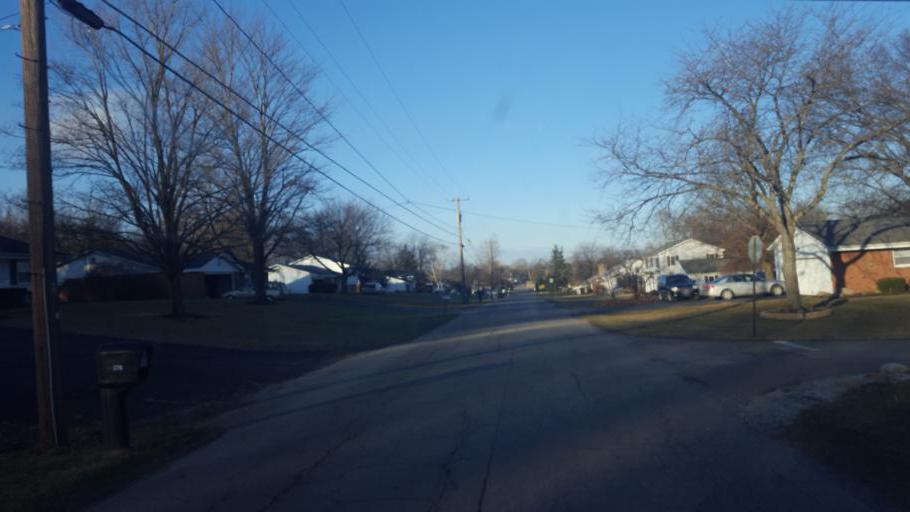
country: US
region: Ohio
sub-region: Morrow County
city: Mount Gilead
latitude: 40.5533
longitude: -82.8406
